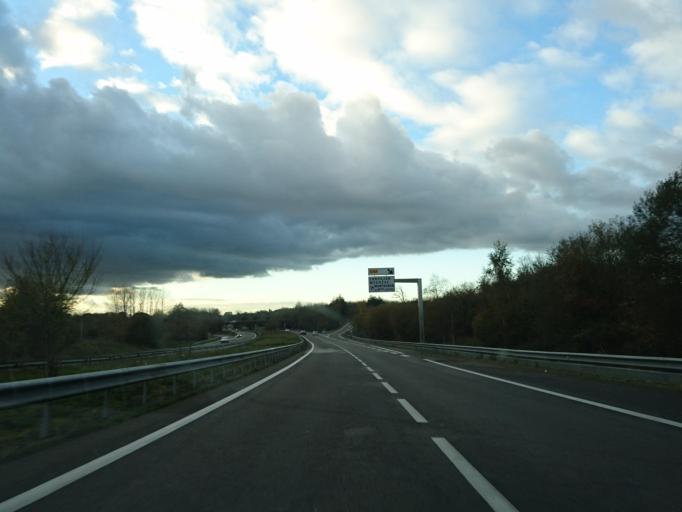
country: FR
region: Brittany
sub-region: Departement d'Ille-et-Vilaine
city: Montauban-de-Bretagne
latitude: 48.2068
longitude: -2.0409
